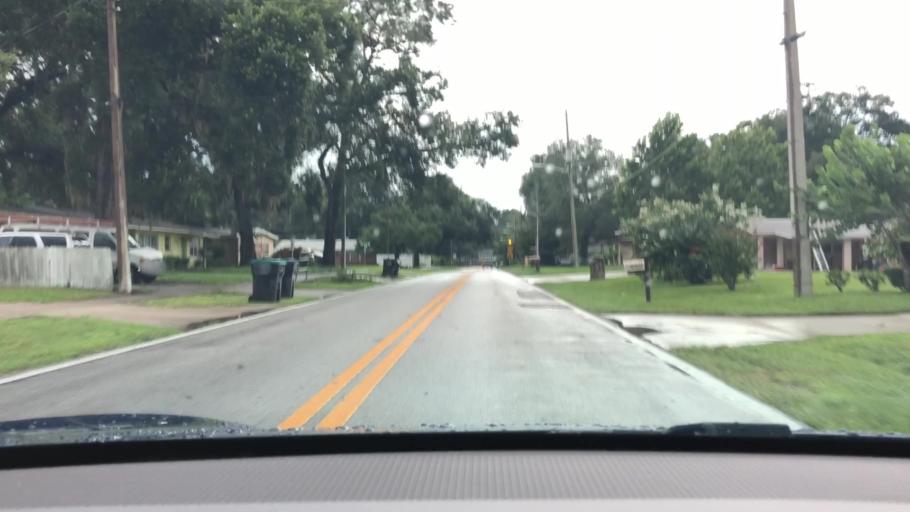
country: US
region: Florida
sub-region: Orange County
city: Conway
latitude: 28.5132
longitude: -81.3463
